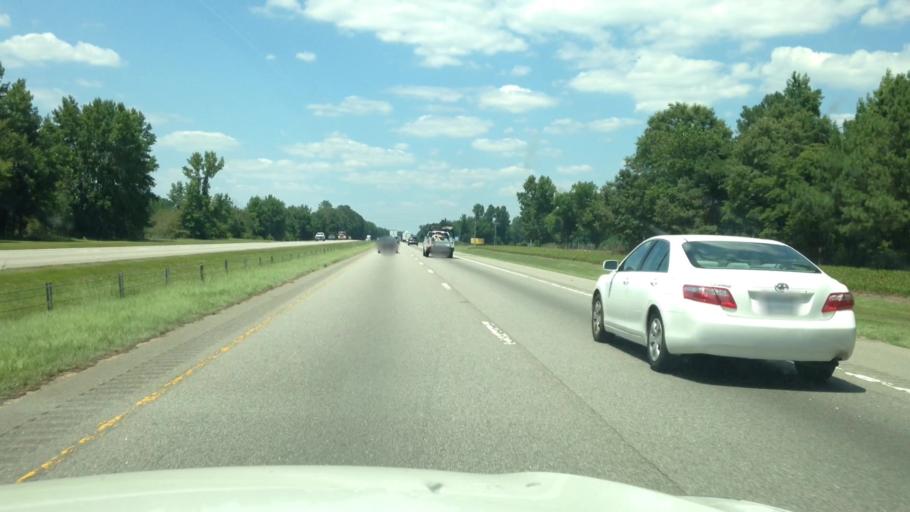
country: US
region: North Carolina
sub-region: Cumberland County
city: Hope Mills
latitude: 34.8895
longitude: -78.9601
